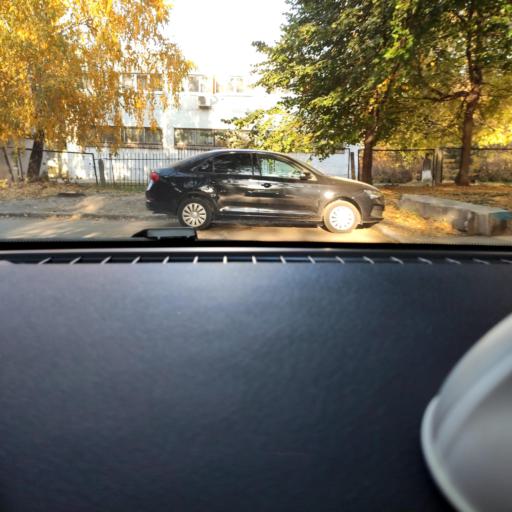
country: RU
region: Samara
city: Samara
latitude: 53.2074
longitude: 50.1398
